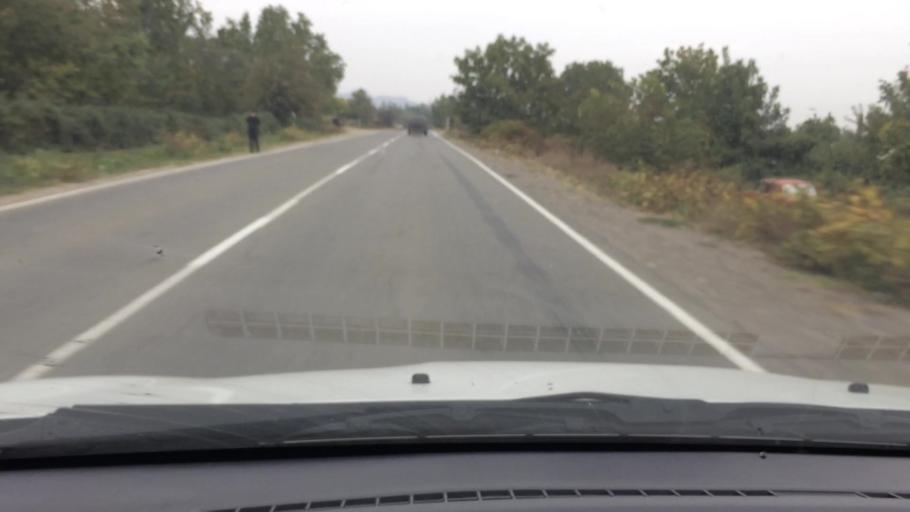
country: GE
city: Naghvarevi
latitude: 41.2994
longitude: 44.7891
